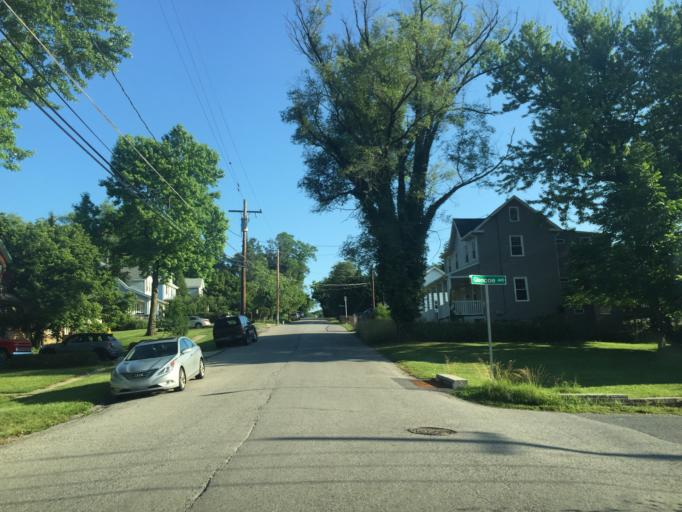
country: US
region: Maryland
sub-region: Baltimore County
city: Catonsville
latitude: 39.2699
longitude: -76.7239
